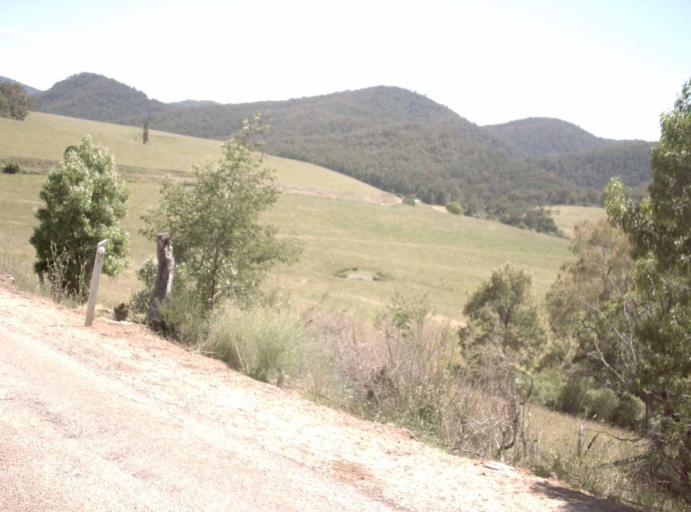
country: AU
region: Victoria
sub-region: East Gippsland
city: Lakes Entrance
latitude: -37.4001
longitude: 148.2143
